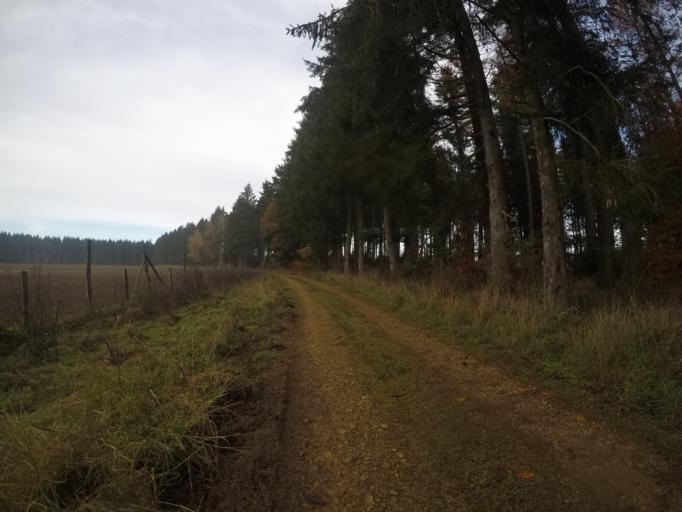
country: BE
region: Wallonia
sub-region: Province du Luxembourg
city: Habay-la-Vieille
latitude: 49.7360
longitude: 5.5988
